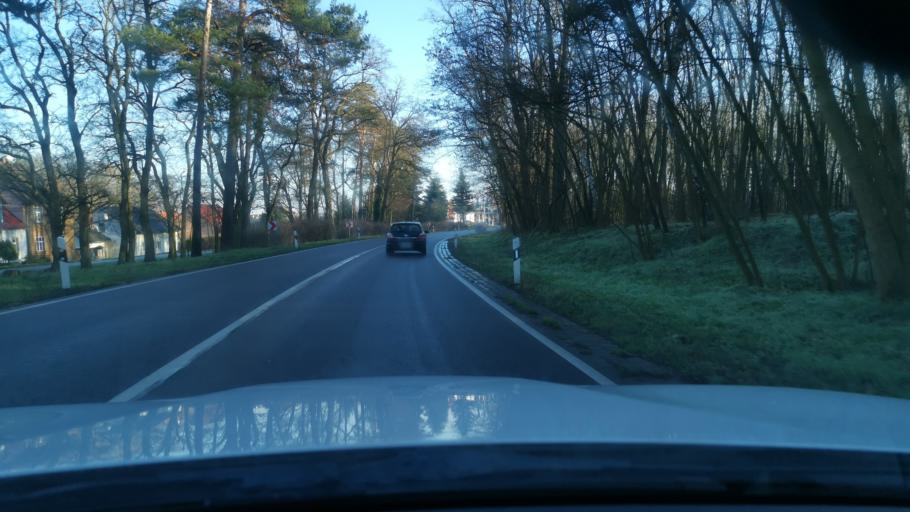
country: DE
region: Saxony-Anhalt
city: Kropstadt
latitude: 51.9584
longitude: 12.7404
